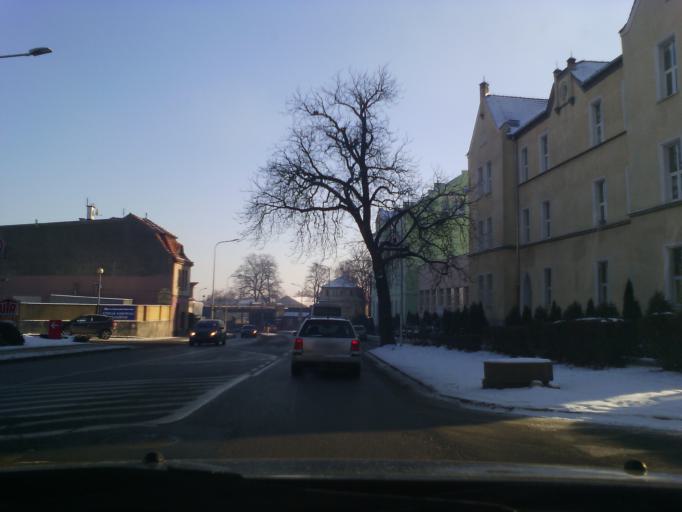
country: PL
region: Lower Silesian Voivodeship
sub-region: Powiat swidnicki
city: Strzegom
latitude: 50.9613
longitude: 16.3494
